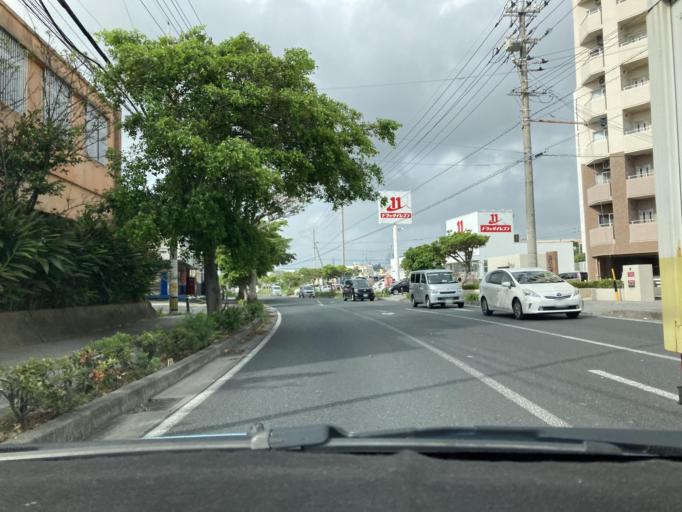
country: JP
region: Okinawa
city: Itoman
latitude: 26.1463
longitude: 127.6735
